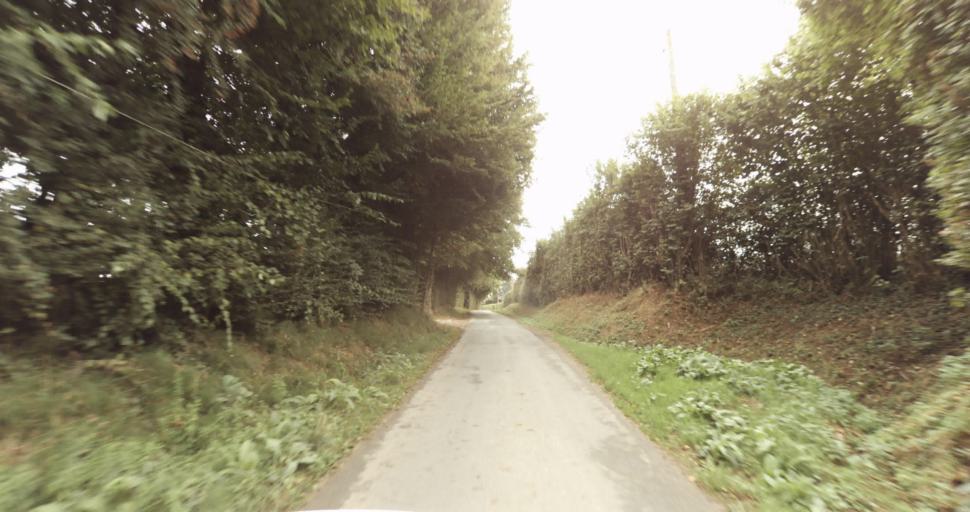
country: FR
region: Lower Normandy
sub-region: Departement du Calvados
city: Livarot
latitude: 48.9402
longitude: 0.1076
